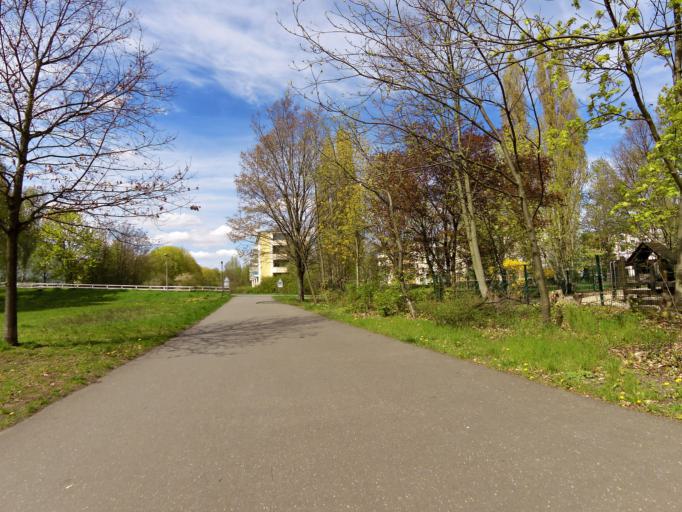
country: DE
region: Berlin
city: Baumschulenweg
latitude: 52.4679
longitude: 13.4759
